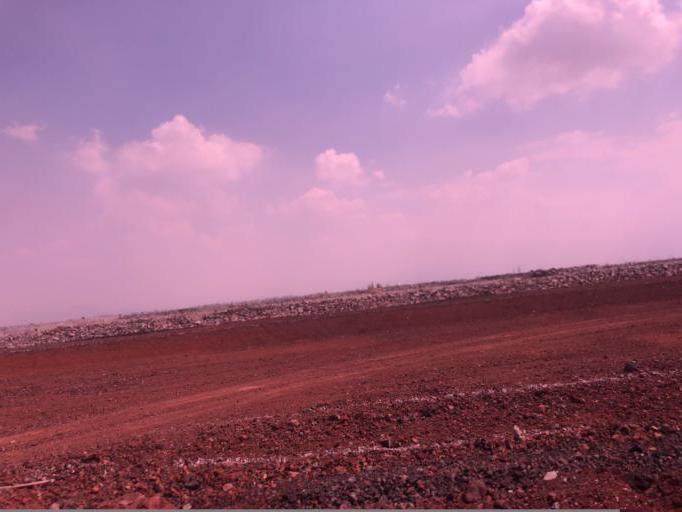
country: MX
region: Mexico
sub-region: Atenco
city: Colonia el Salado
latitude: 19.5363
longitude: -98.9939
